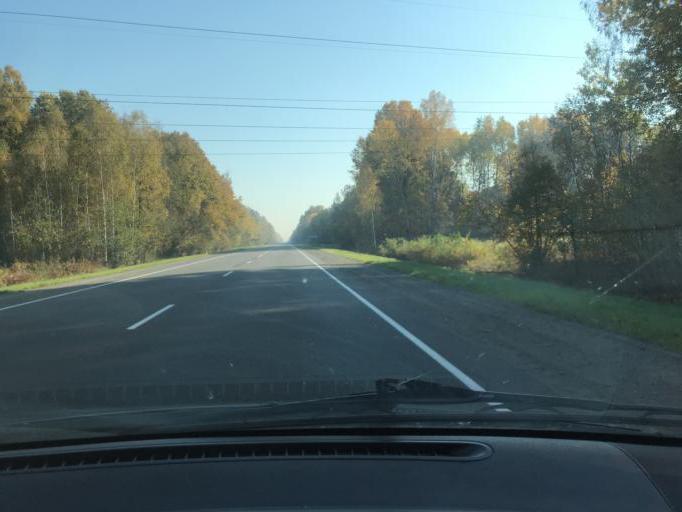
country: BY
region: Brest
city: Horad Luninyets
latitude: 52.3082
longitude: 26.6824
